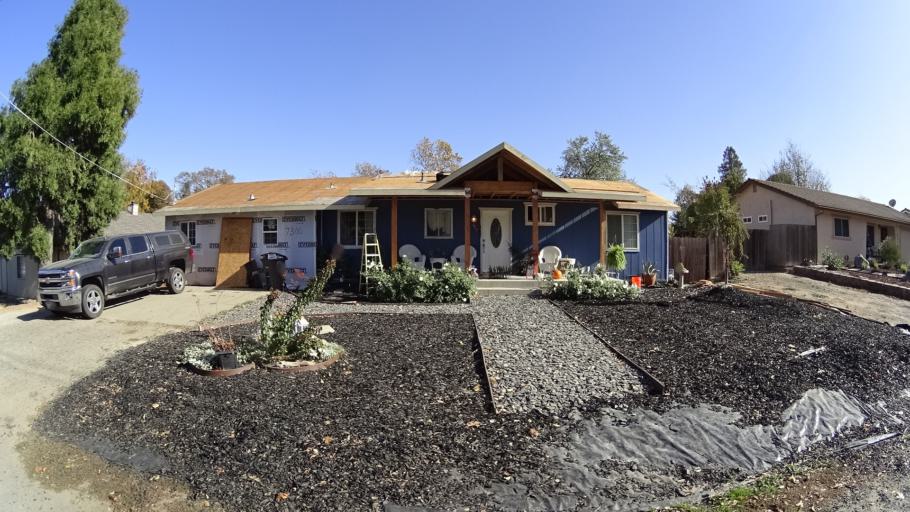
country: US
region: California
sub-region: Sacramento County
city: Citrus Heights
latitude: 38.6985
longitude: -121.2853
